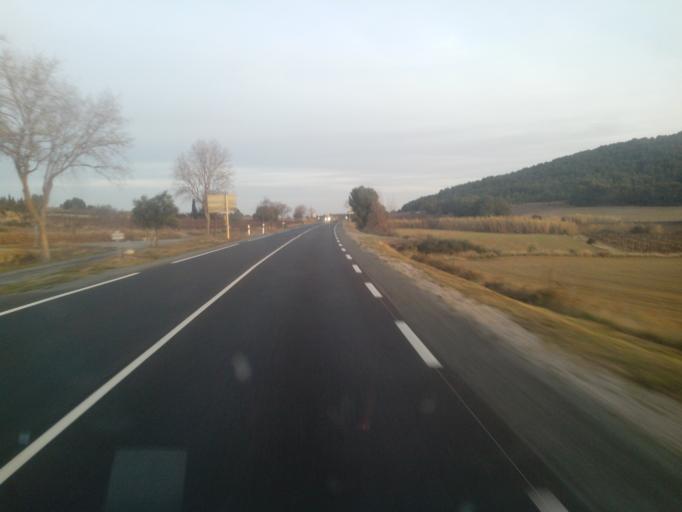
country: FR
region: Languedoc-Roussillon
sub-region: Departement de l'Herault
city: Olonzac
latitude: 43.2751
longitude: 2.7740
